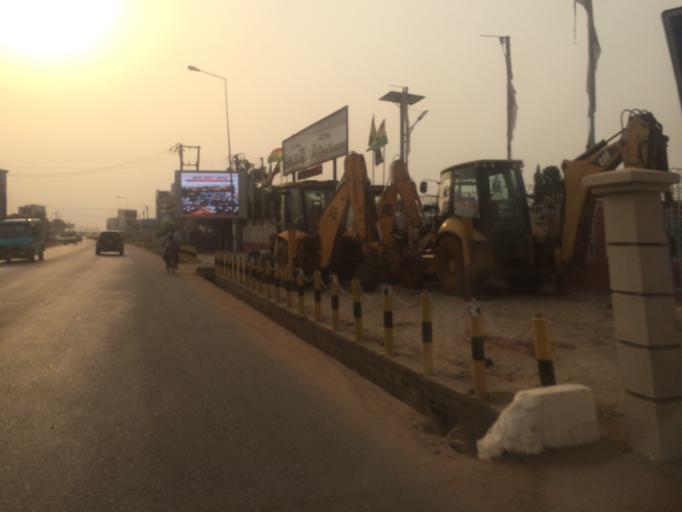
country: GH
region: Greater Accra
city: Nungua
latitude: 5.6361
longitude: -0.1027
